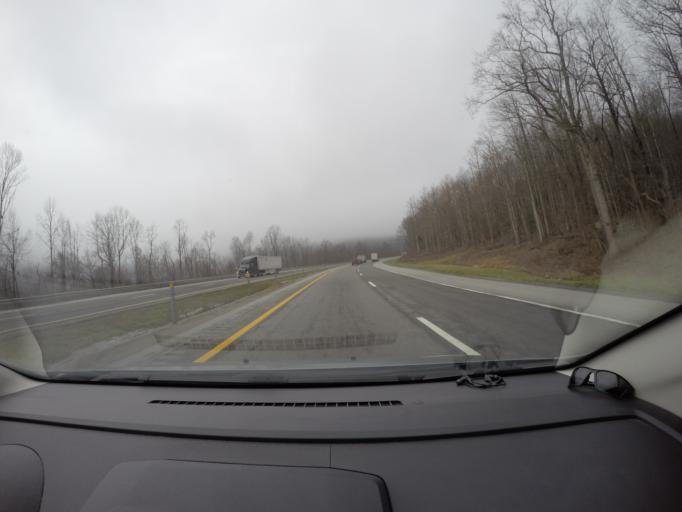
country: US
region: Tennessee
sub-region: Marion County
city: Monteagle
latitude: 35.2463
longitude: -85.8728
